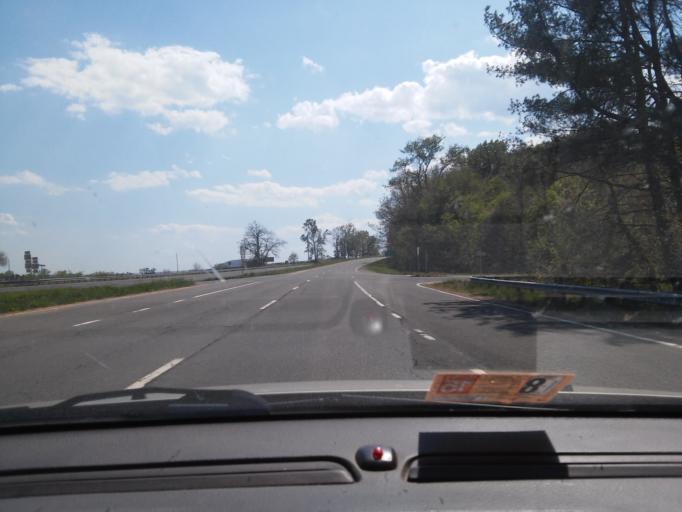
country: US
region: Virginia
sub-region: Rappahannock County
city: Washington
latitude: 38.6987
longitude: -78.1632
